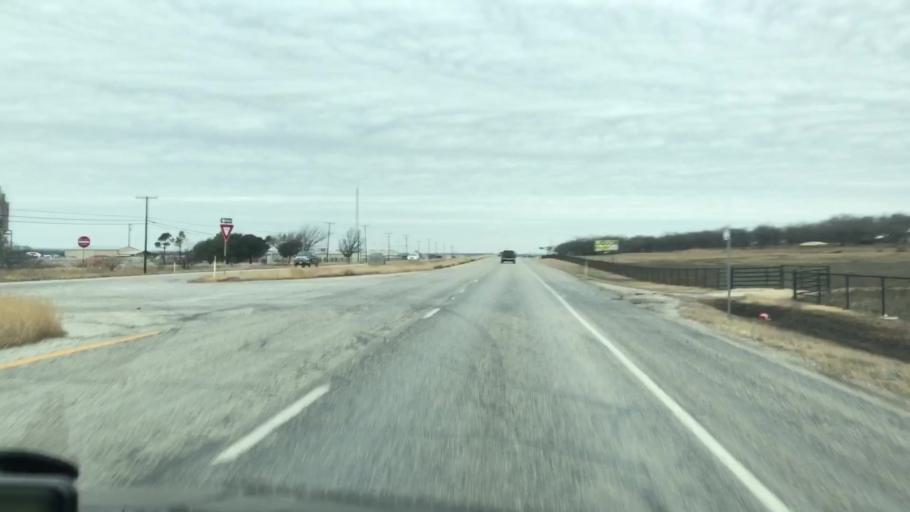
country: US
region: Texas
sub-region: Jack County
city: Jacksboro
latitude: 33.1930
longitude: -98.1405
